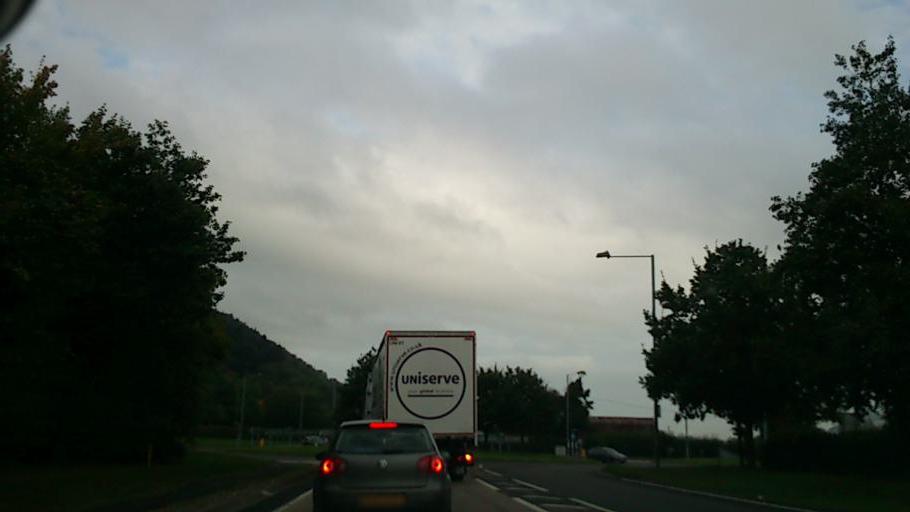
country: GB
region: Wales
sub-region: Sir Powys
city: Welshpool
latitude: 52.6716
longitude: -3.1223
